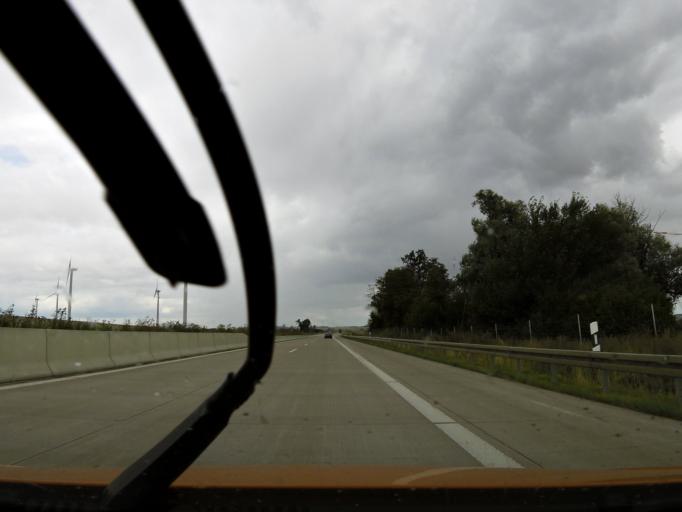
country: DE
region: Brandenburg
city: Gramzow
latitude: 53.2674
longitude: 14.0447
